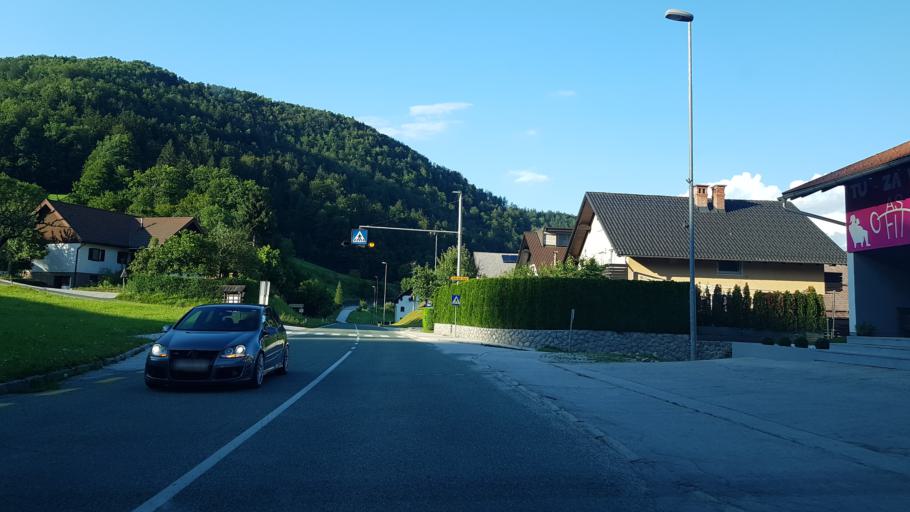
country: SI
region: Gorenja Vas-Poljane
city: Gorenja Vas
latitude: 46.1301
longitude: 14.2270
